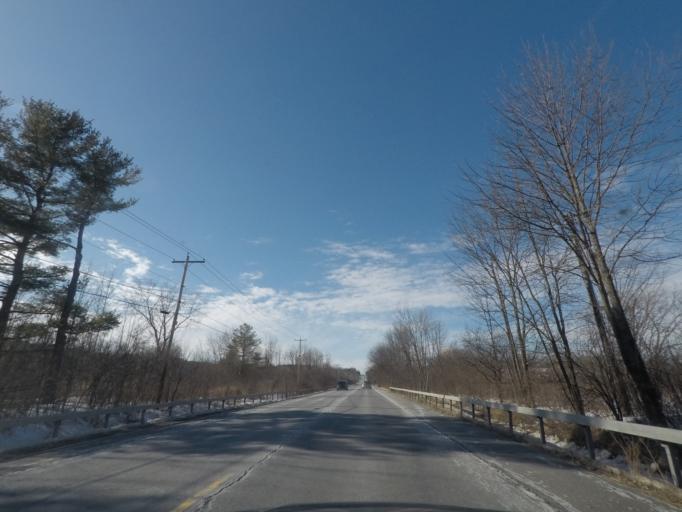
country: US
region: New York
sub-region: Albany County
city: Altamont
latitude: 42.7441
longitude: -74.0286
